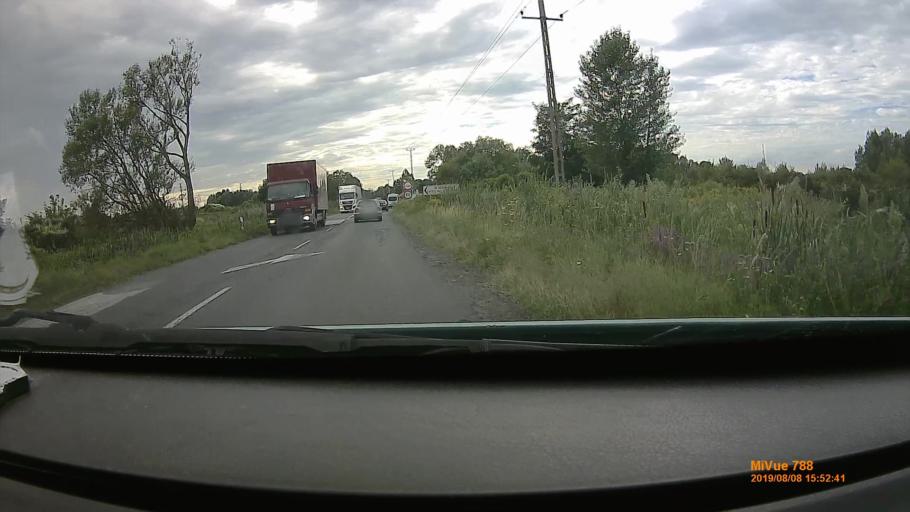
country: HU
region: Szabolcs-Szatmar-Bereg
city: Mateszalka
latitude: 47.9399
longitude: 22.3310
